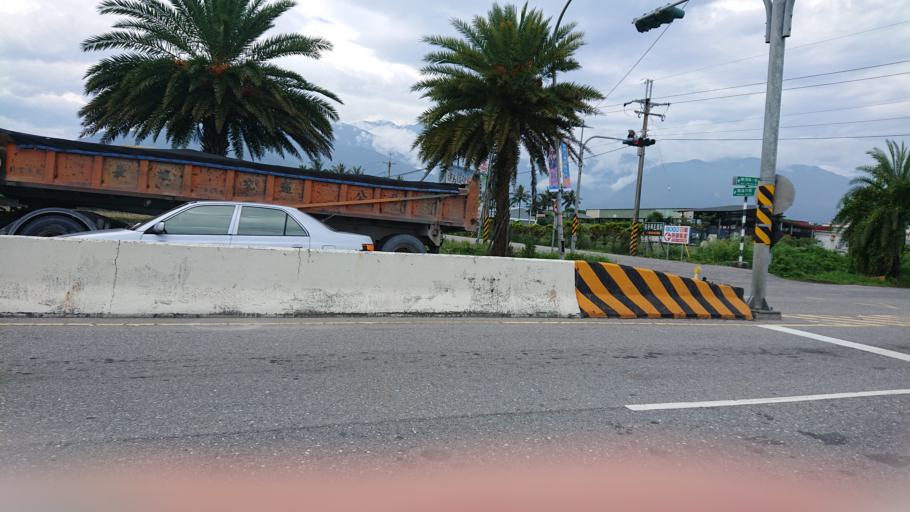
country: TW
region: Taiwan
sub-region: Hualien
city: Hualian
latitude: 23.9460
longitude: 121.5972
